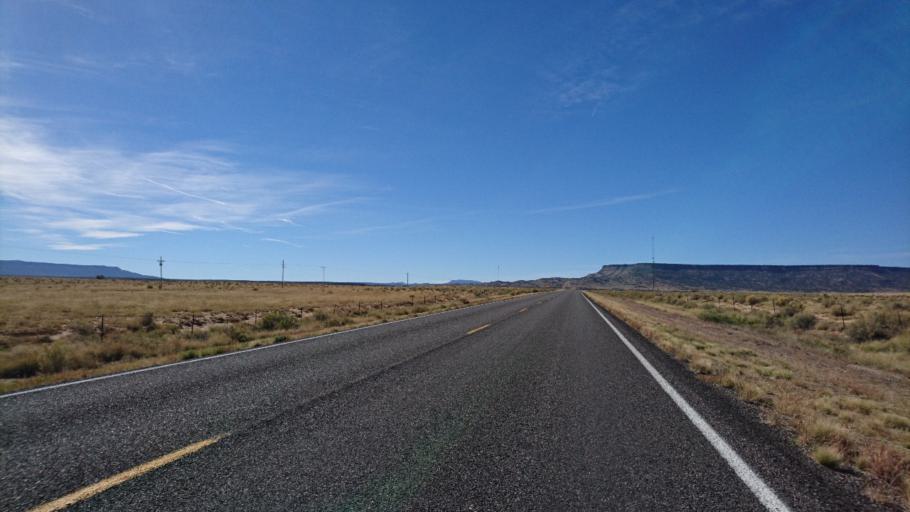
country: US
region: New Mexico
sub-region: Cibola County
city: Skyline-Ganipa
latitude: 35.0824
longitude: -107.6214
